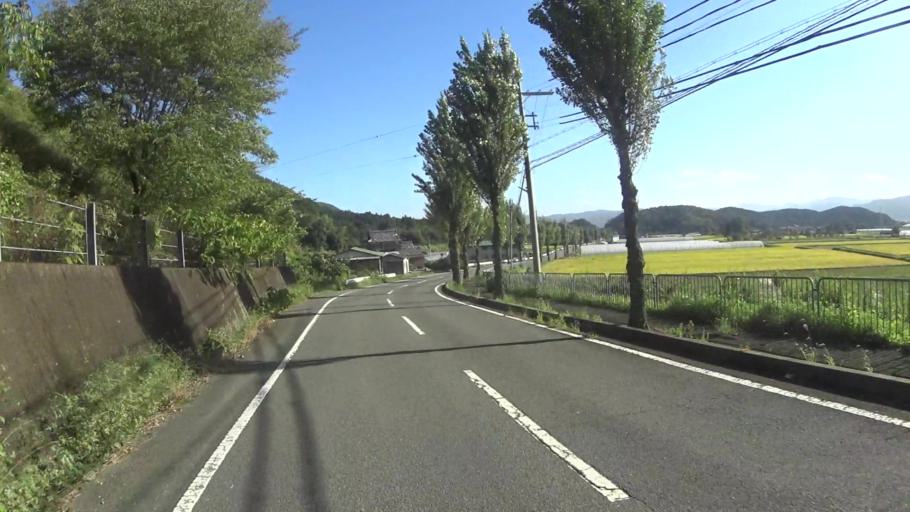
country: JP
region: Kyoto
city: Kameoka
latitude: 35.0828
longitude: 135.5653
